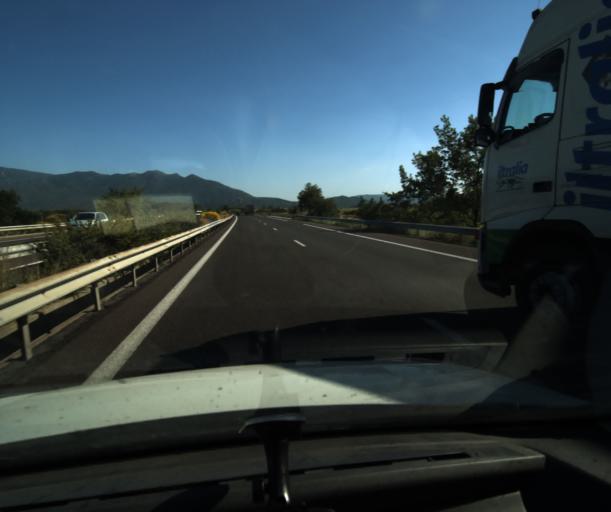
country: FR
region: Languedoc-Roussillon
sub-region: Departement des Pyrenees-Orientales
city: Banyuls-dels-Aspres
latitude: 42.5629
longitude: 2.8448
